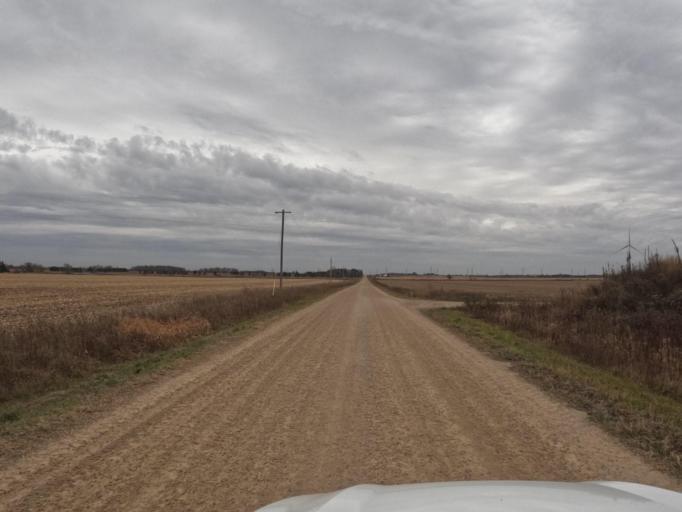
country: CA
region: Ontario
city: Shelburne
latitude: 44.0158
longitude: -80.3906
